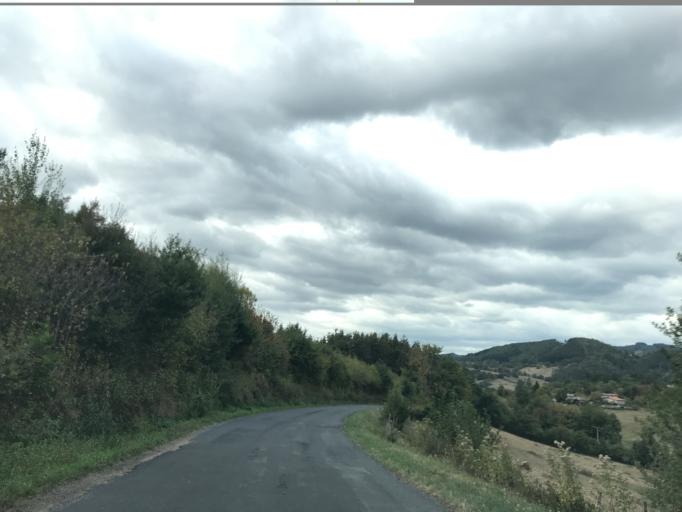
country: FR
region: Auvergne
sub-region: Departement du Puy-de-Dome
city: Escoutoux
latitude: 45.7785
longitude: 3.5913
